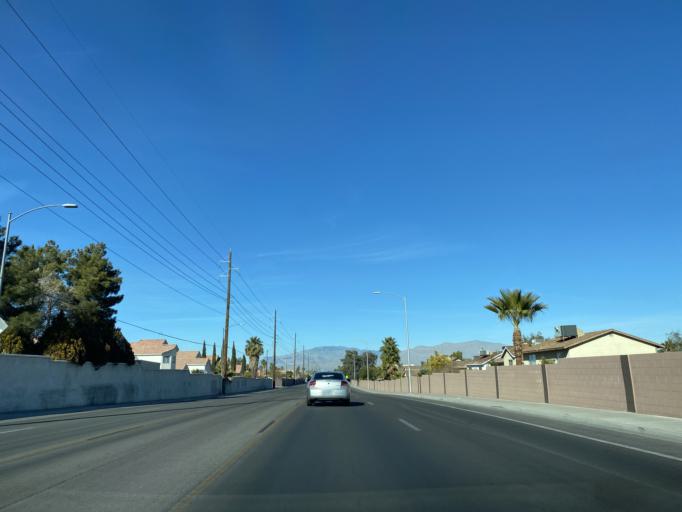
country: US
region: Nevada
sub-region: Clark County
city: Spring Valley
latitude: 36.1853
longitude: -115.2510
